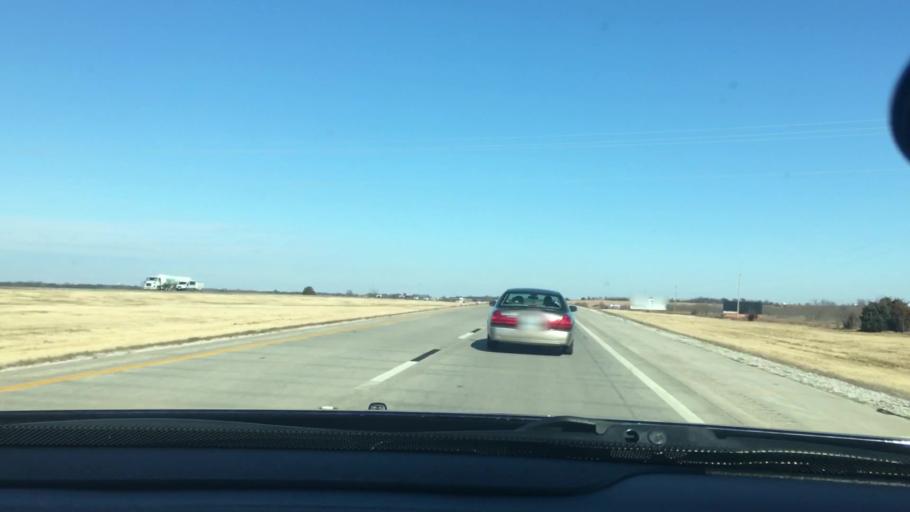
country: US
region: Oklahoma
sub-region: Carter County
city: Ardmore
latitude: 34.0960
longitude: -97.1507
